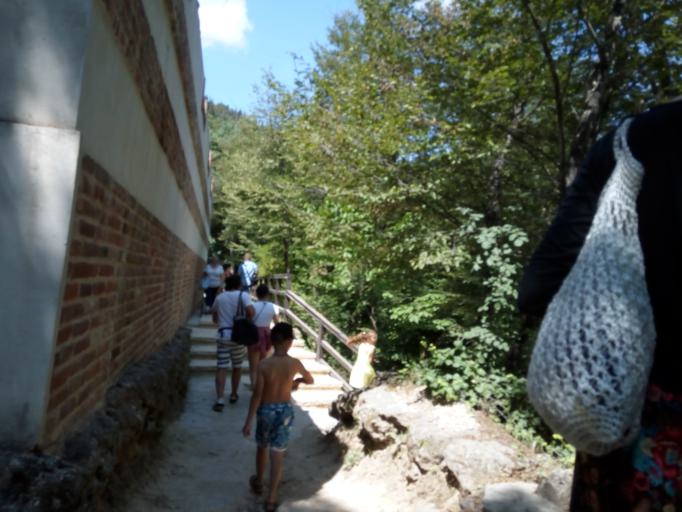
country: HR
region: Sibensko-Kniniska
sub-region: Grad Sibenik
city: Sibenik
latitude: 43.8047
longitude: 15.9638
